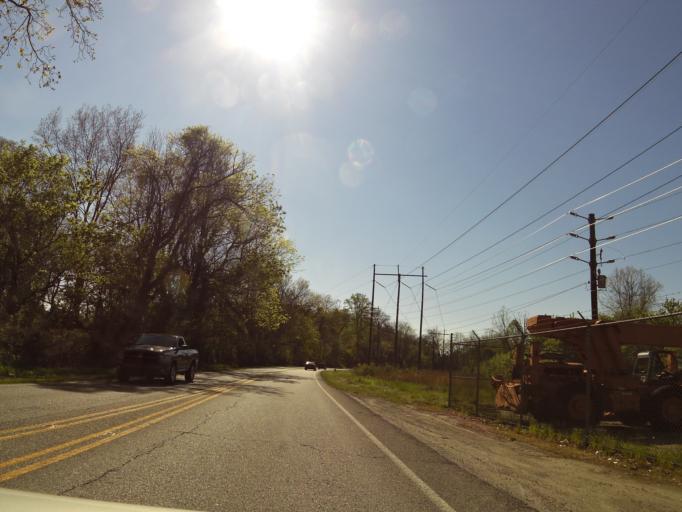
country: US
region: North Carolina
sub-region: Buncombe County
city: Asheville
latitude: 35.5637
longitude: -82.5604
